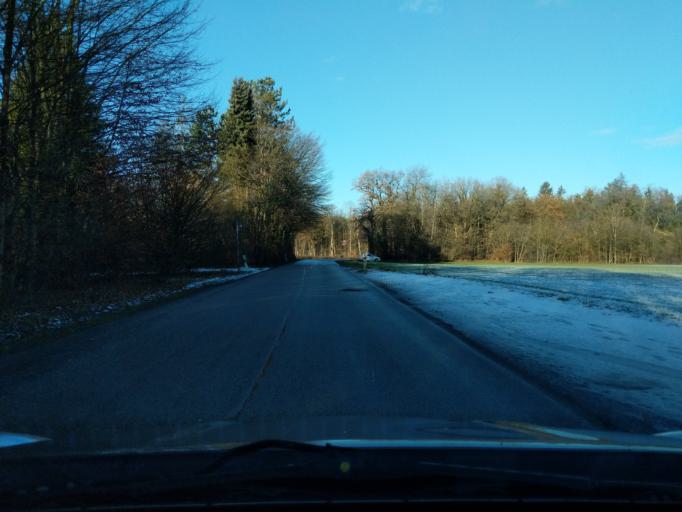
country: DE
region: Bavaria
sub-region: Upper Bavaria
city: Zorneding
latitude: 48.0863
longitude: 11.8534
